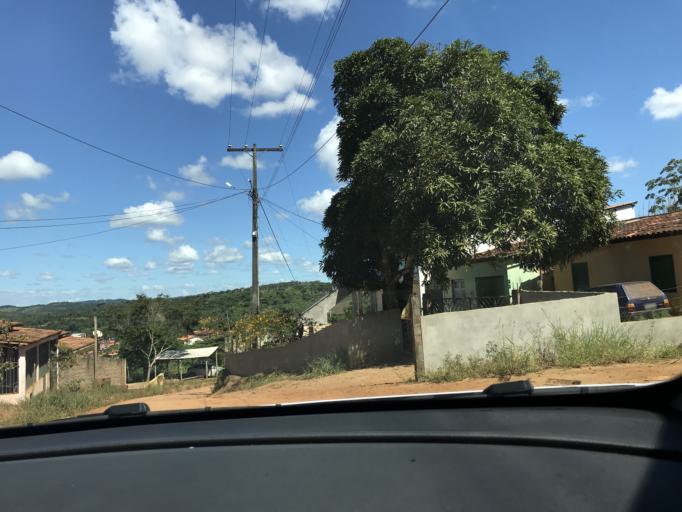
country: BR
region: Bahia
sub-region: Valenca
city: Valenca
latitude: -13.3214
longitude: -39.2407
